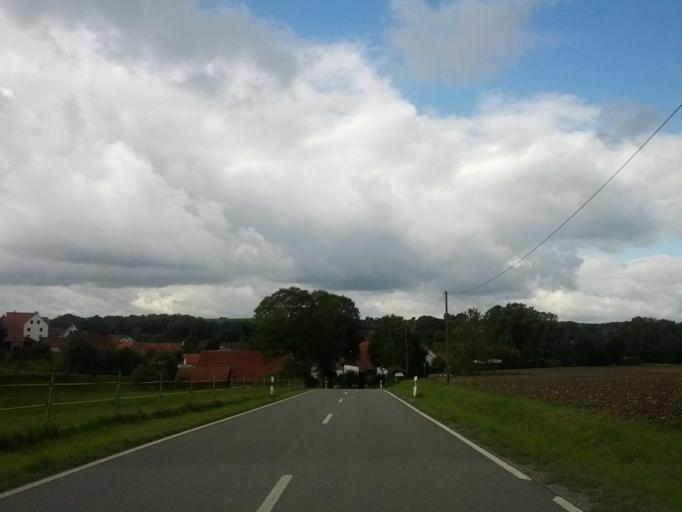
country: DE
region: Hesse
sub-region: Regierungsbezirk Kassel
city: Weissenborn
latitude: 51.0665
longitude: 10.0812
